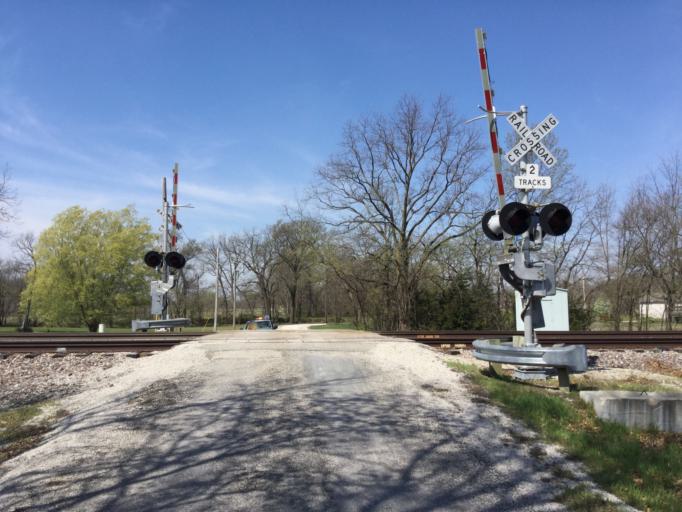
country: US
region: Kansas
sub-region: Neosho County
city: Erie
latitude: 37.5616
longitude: -95.2362
